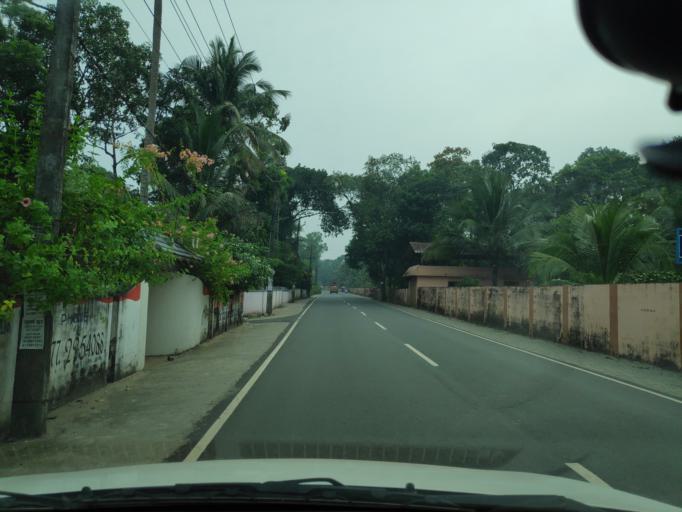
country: IN
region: Kerala
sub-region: Alappuzha
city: Shertallai
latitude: 9.6084
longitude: 76.3378
